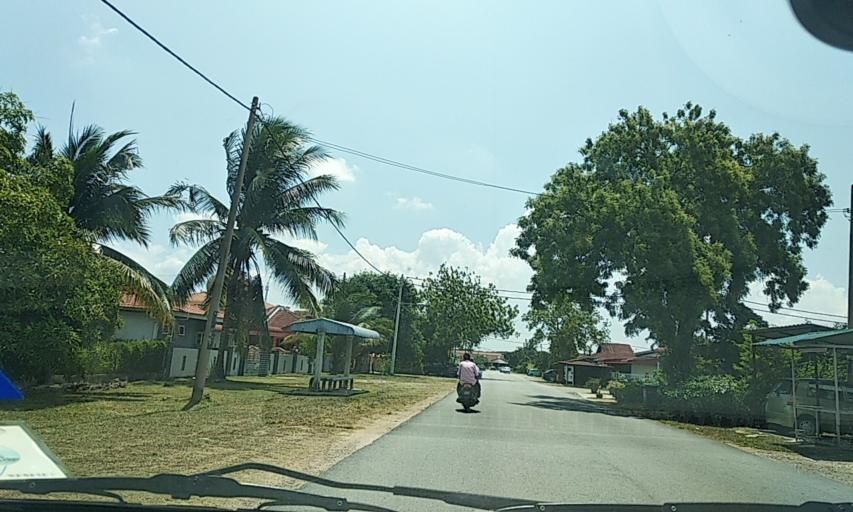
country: MY
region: Kedah
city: Sungai Petani
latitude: 5.6341
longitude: 100.4709
